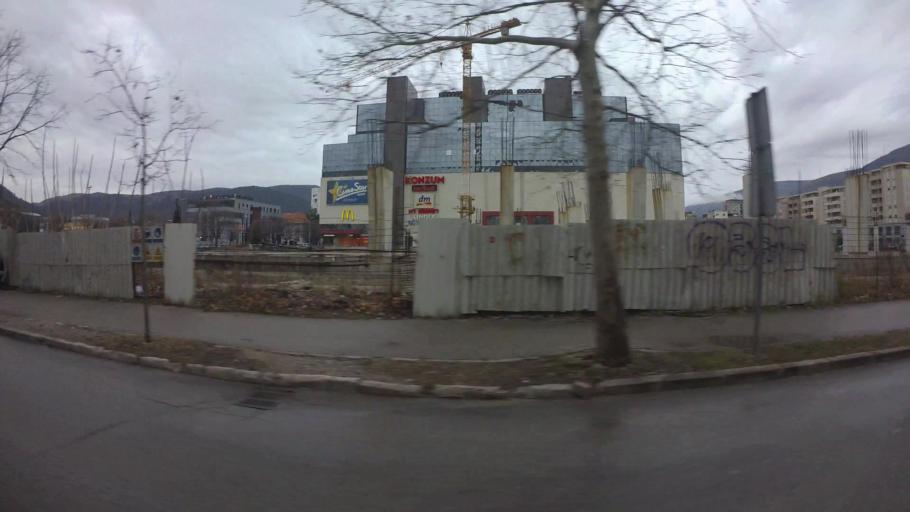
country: BA
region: Federation of Bosnia and Herzegovina
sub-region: Hercegovacko-Bosanski Kanton
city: Mostar
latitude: 43.3486
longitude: 17.8067
